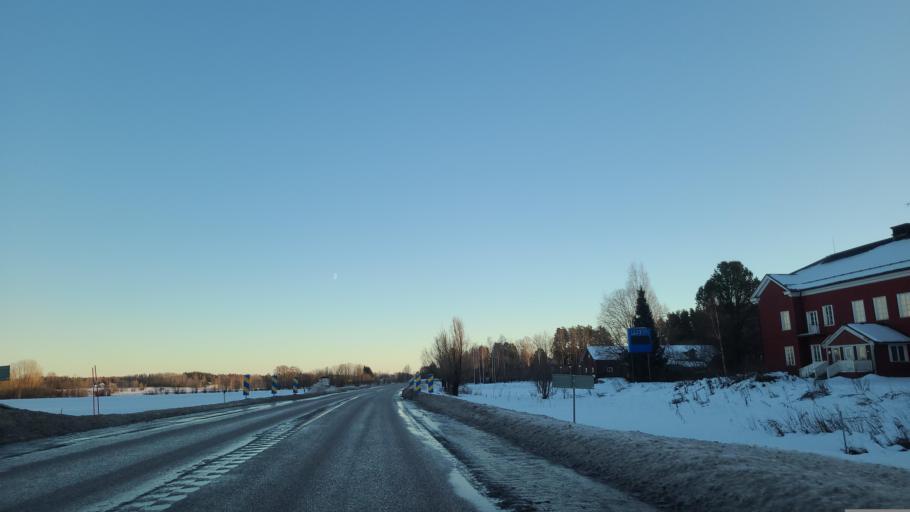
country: SE
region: Gaevleborg
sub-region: Soderhamns Kommun
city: Soderhamn
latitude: 61.2908
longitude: 16.8854
